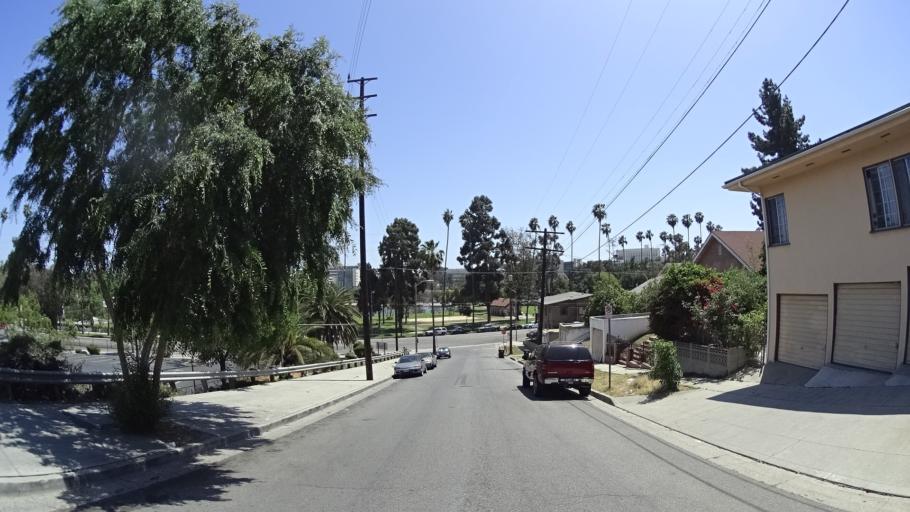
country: US
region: California
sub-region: Los Angeles County
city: Boyle Heights
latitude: 34.0680
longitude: -118.2039
